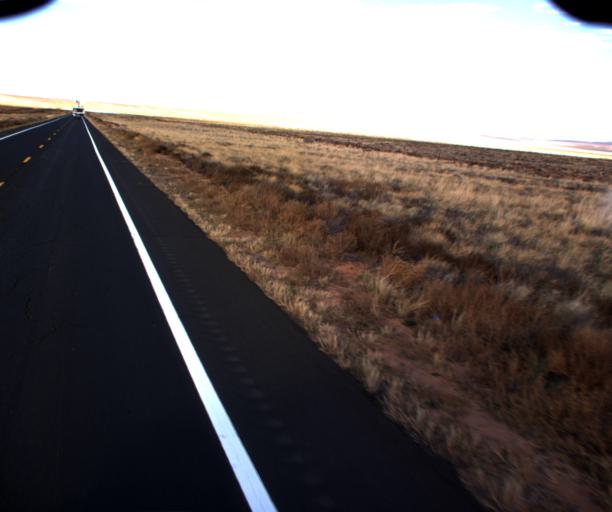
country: US
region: Arizona
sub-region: Apache County
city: Lukachukai
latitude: 36.9618
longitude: -109.4114
